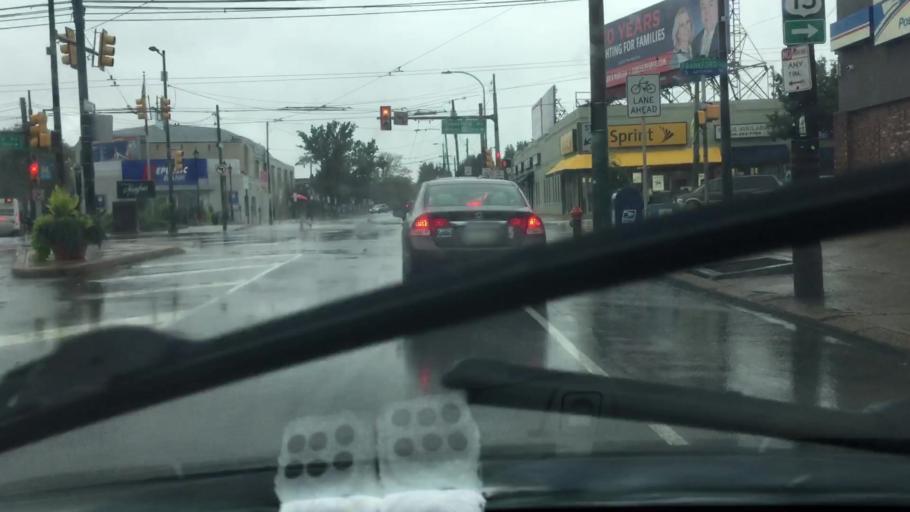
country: US
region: New Jersey
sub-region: Burlington County
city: Palmyra
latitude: 40.0366
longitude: -75.0404
